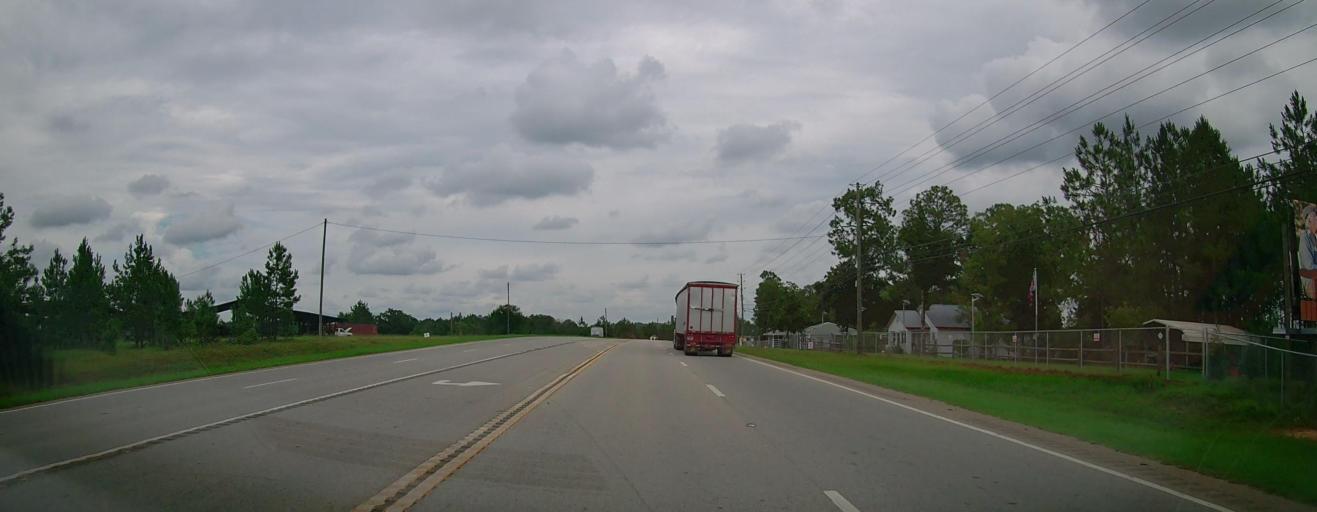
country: US
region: Georgia
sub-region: Jeff Davis County
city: Hazlehurst
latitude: 31.8951
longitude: -82.6140
